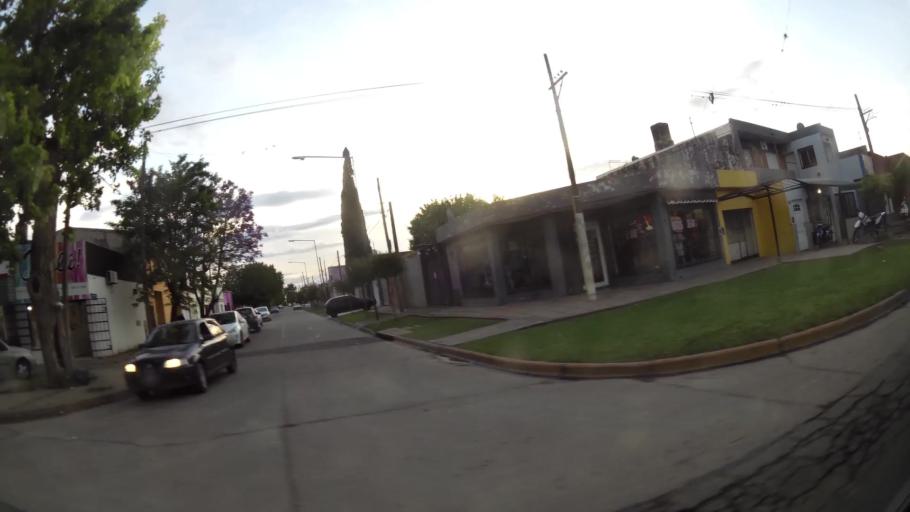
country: AR
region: Buenos Aires
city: San Nicolas de los Arroyos
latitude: -33.3155
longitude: -60.2334
